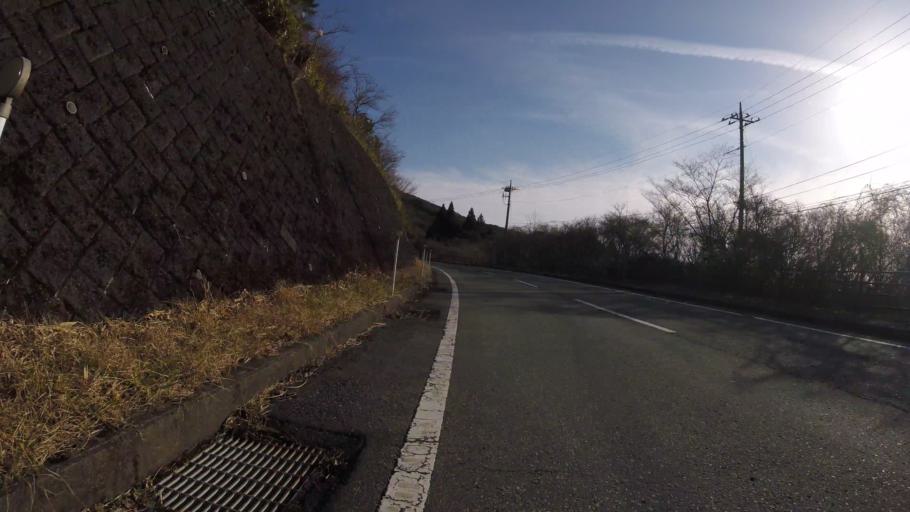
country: JP
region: Kanagawa
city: Hakone
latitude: 35.1757
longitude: 139.0208
